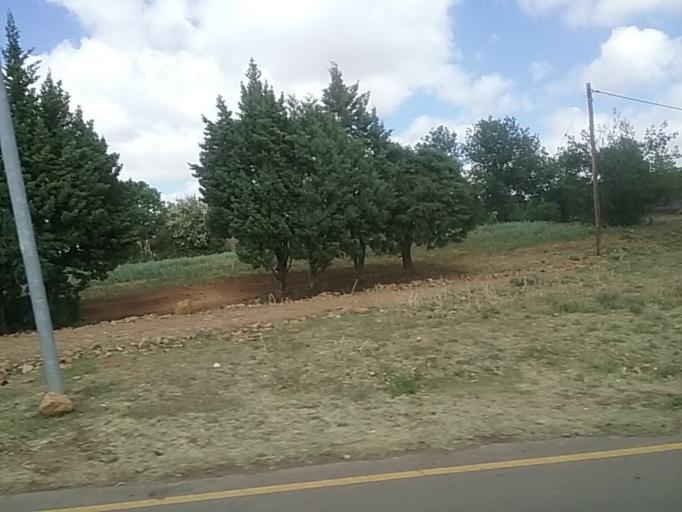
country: LS
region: Berea
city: Teyateyaneng
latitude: -29.1380
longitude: 27.7349
